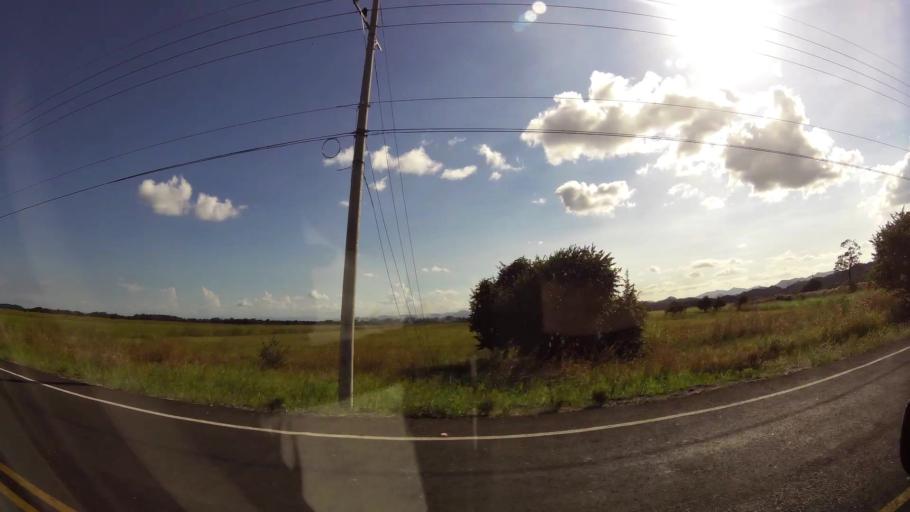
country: CR
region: Guanacaste
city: Sardinal
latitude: 10.5666
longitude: -85.6153
